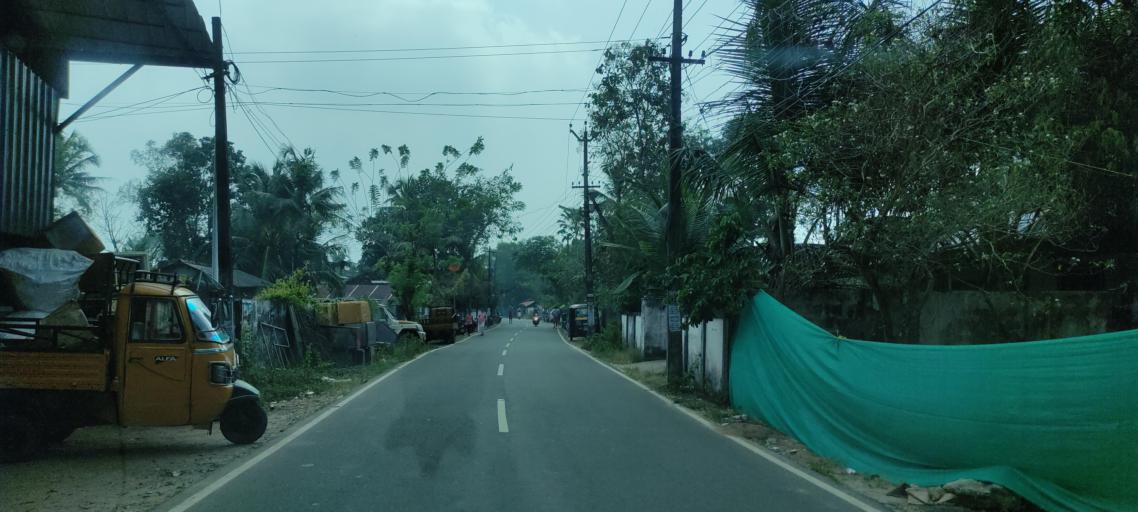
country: IN
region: Kerala
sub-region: Alappuzha
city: Alleppey
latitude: 9.5667
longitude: 76.3352
